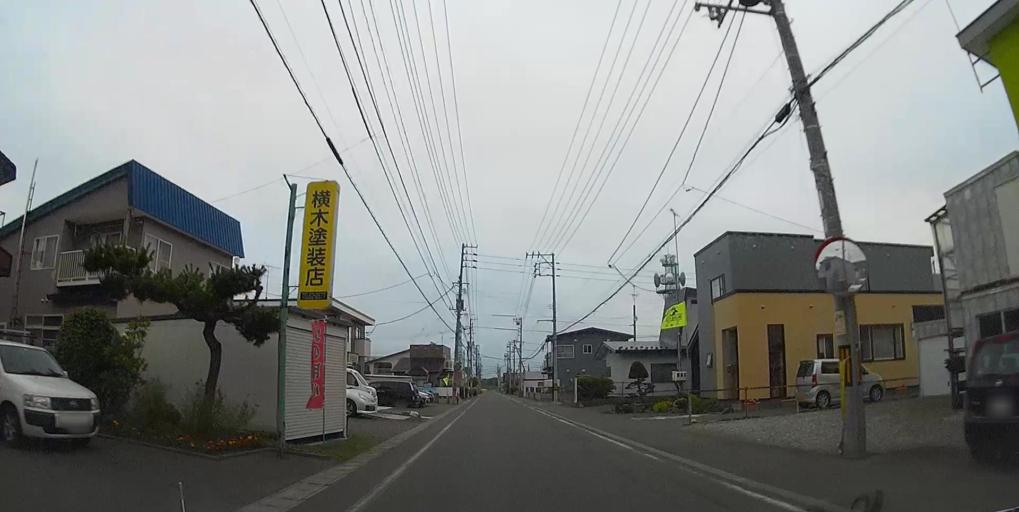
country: JP
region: Hokkaido
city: Nanae
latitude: 42.2591
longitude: 140.2710
